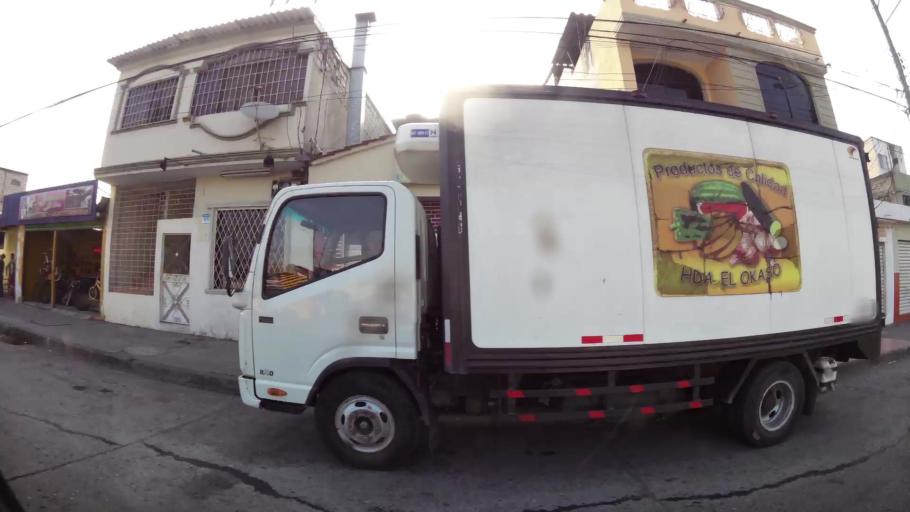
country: EC
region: Guayas
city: Eloy Alfaro
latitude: -2.1285
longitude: -79.9014
